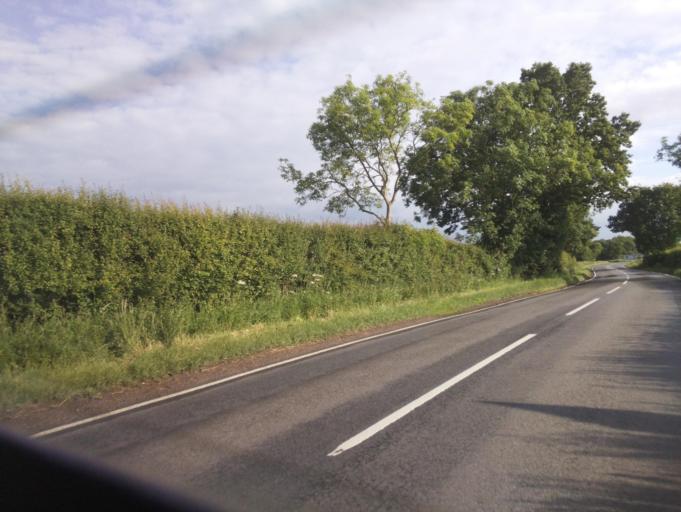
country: GB
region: England
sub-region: Lincolnshire
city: Great Gonerby
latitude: 53.0531
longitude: -0.6440
